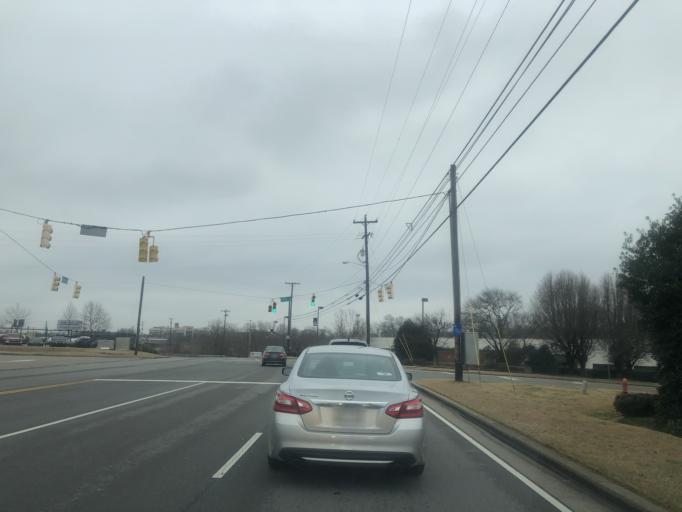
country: US
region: Tennessee
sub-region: Davidson County
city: Lakewood
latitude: 36.1472
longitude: -86.6725
